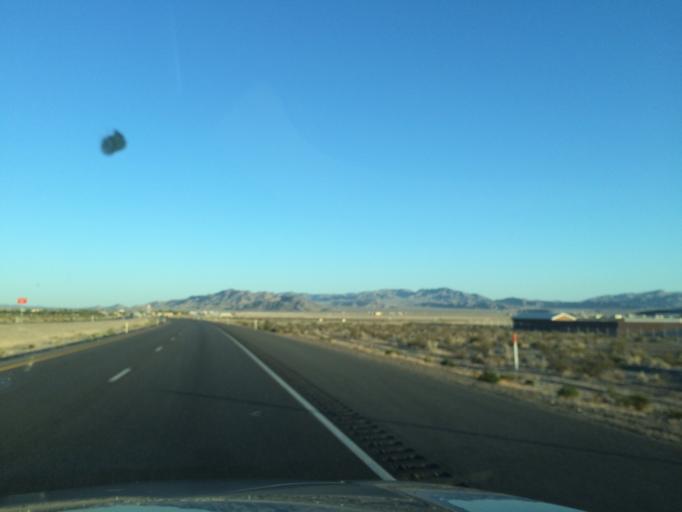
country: US
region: Nevada
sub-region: Nye County
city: Pahrump
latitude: 36.5764
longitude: -115.6441
